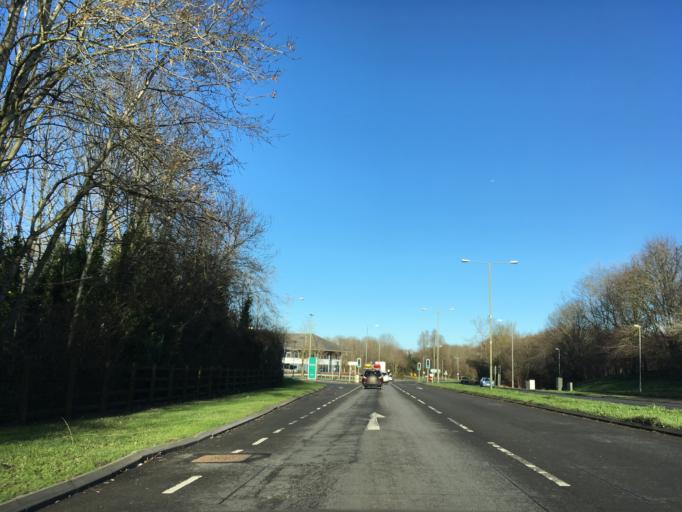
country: GB
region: England
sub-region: Wiltshire
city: Lydiard Tregoze
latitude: 51.5486
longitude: -1.8441
